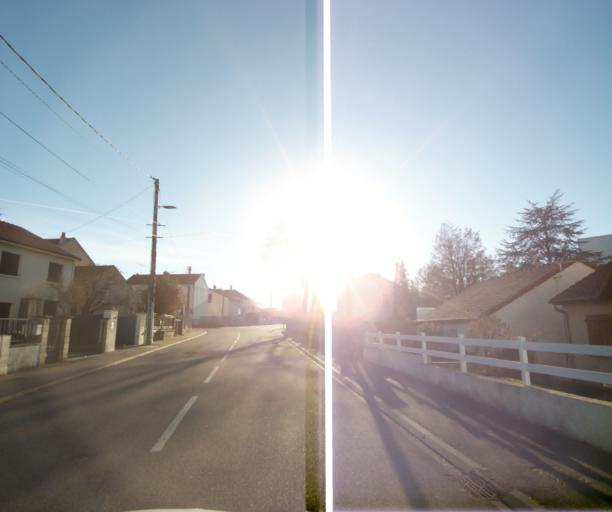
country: FR
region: Lorraine
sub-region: Departement de Meurthe-et-Moselle
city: Laneuveville-devant-Nancy
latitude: 48.6550
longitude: 6.2272
